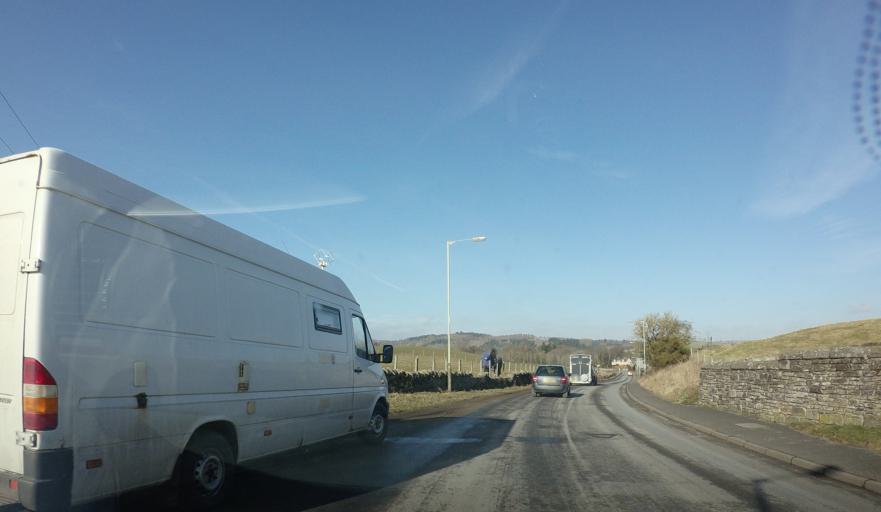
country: GB
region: Scotland
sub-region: Perth and Kinross
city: Bankfoot
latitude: 56.5319
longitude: -3.4700
